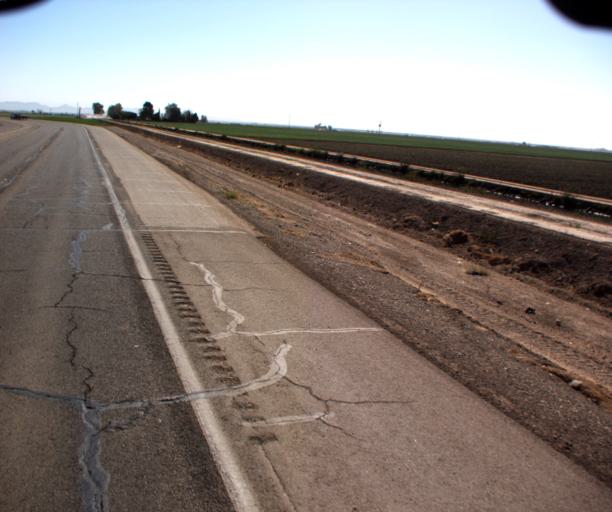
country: US
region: Arizona
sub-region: Yuma County
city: Somerton
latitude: 32.5673
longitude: -114.7756
